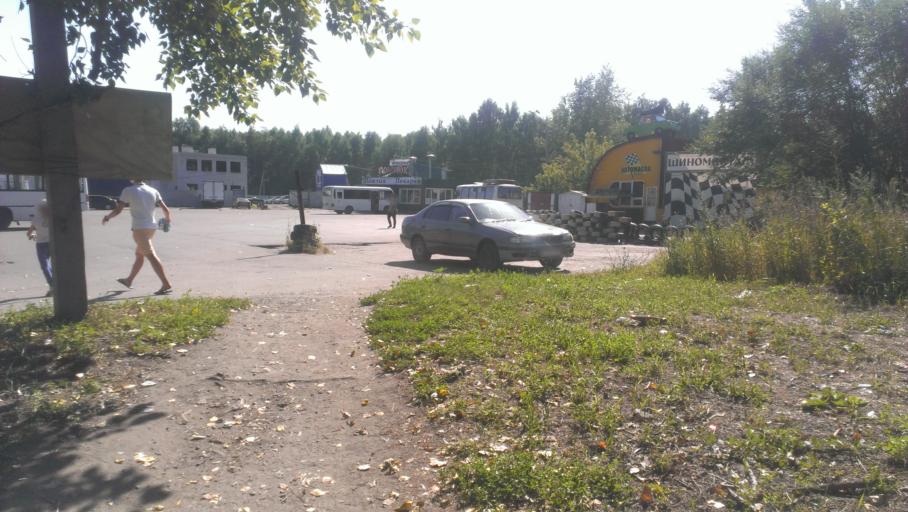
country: RU
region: Altai Krai
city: Novosilikatnyy
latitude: 53.3693
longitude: 83.6617
